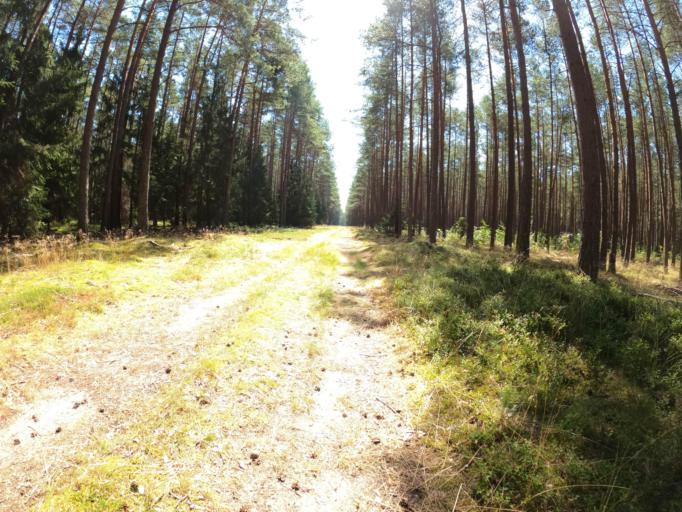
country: PL
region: West Pomeranian Voivodeship
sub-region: Powiat bialogardzki
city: Tychowo
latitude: 54.0644
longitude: 16.3646
